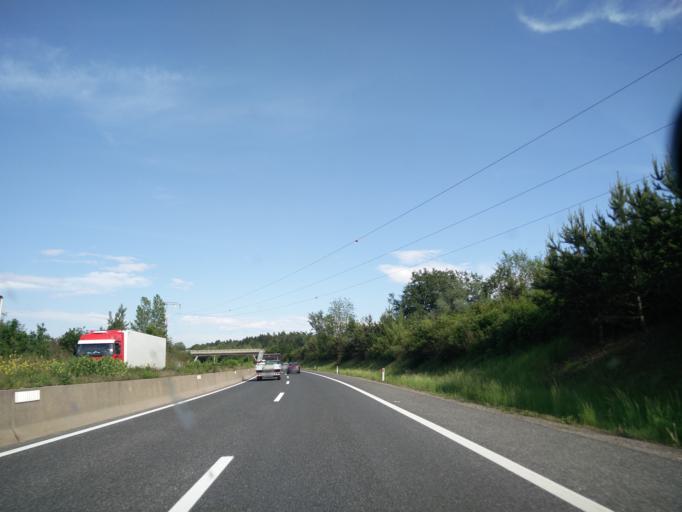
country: AT
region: Carinthia
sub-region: Politischer Bezirk Klagenfurt Land
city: Ebenthal
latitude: 46.6448
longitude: 14.3937
